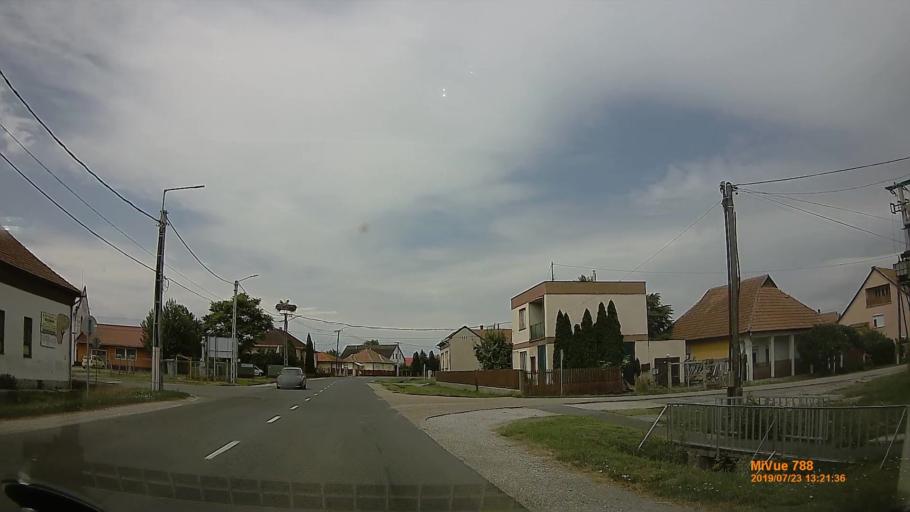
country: HU
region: Hajdu-Bihar
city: Polgar
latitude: 47.8679
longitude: 21.1216
